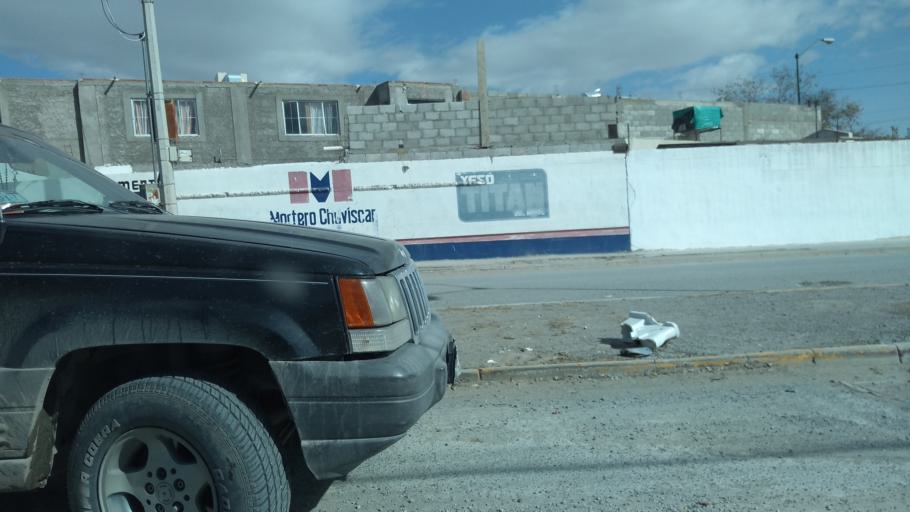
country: US
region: Texas
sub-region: El Paso County
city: San Elizario
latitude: 31.5785
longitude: -106.3469
